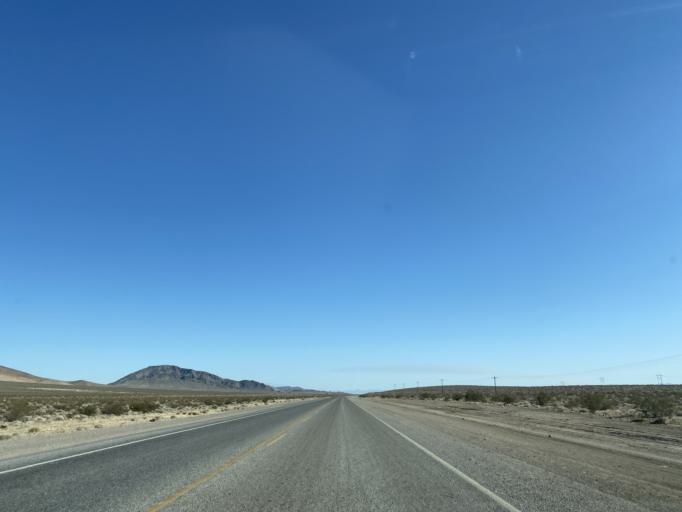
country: US
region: Nevada
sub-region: Nye County
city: Beatty
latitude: 36.7699
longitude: -116.6814
